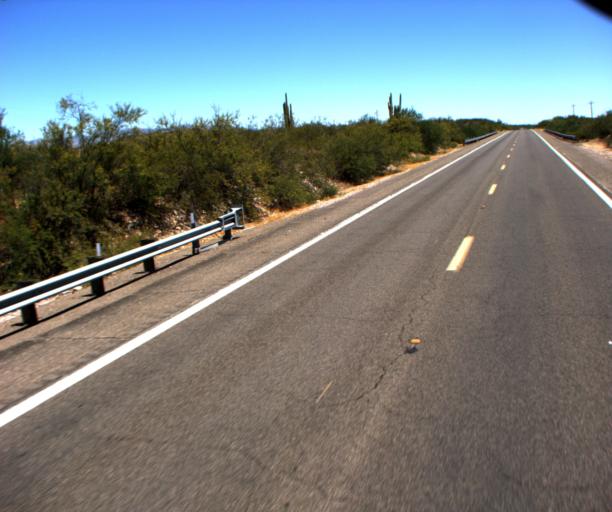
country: US
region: Arizona
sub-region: Pinal County
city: Mammoth
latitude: 32.8087
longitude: -110.6842
